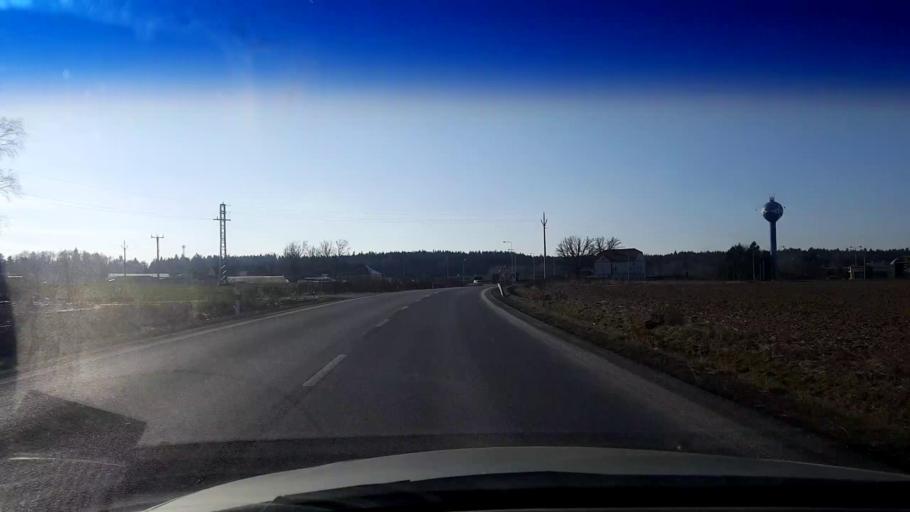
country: CZ
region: Karlovarsky
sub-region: Okres Cheb
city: Cheb
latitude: 50.0487
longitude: 12.3590
